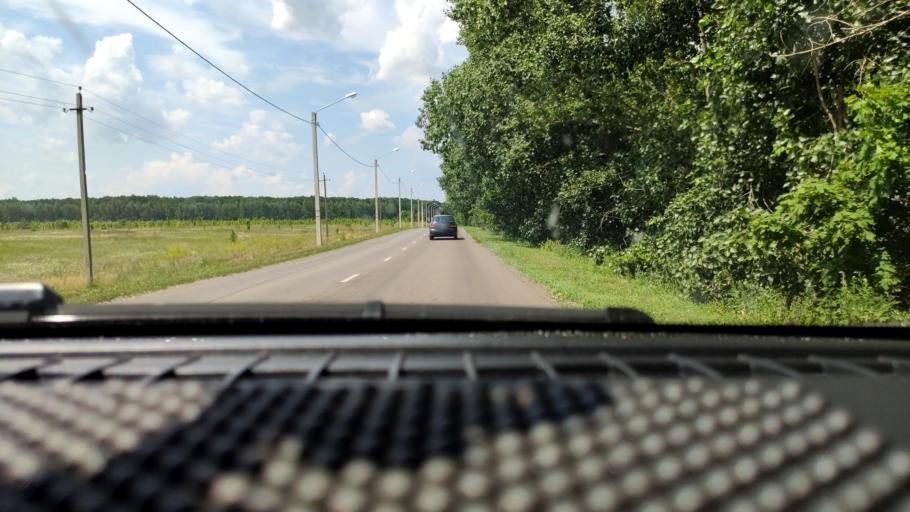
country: RU
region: Voronezj
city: Podkletnoye
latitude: 51.6475
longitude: 39.4708
